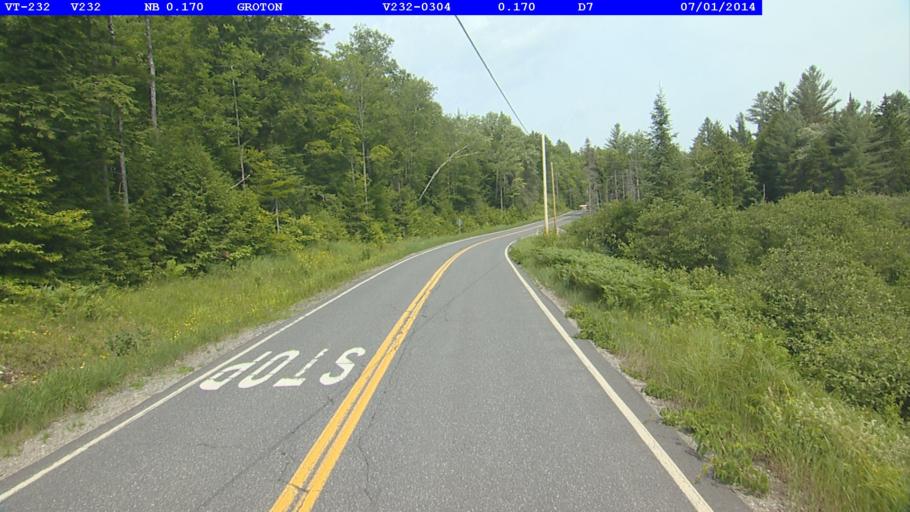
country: US
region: New Hampshire
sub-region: Grafton County
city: Woodsville
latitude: 44.2218
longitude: -72.2270
